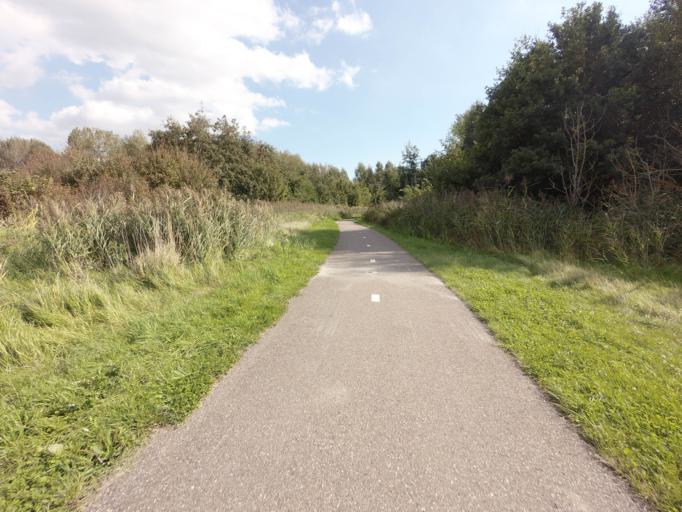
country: NL
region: Zeeland
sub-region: Gemeente Vlissingen
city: Vlissingen
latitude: 51.4781
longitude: 3.5263
